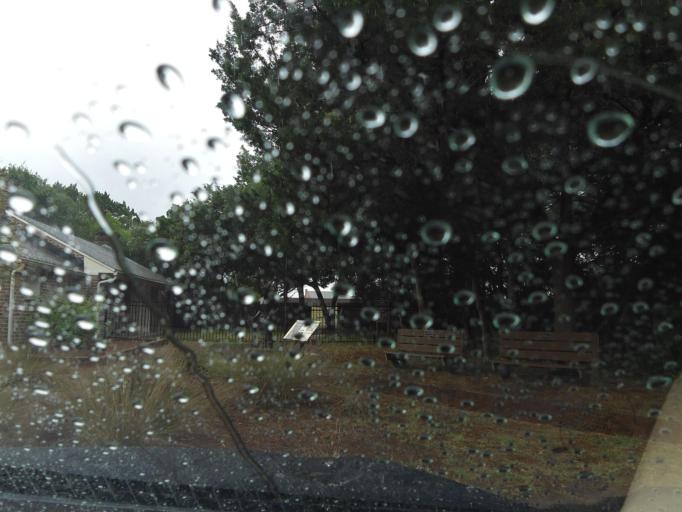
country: US
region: Florida
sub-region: Nassau County
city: Fernandina Beach
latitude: 30.7035
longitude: -81.4533
